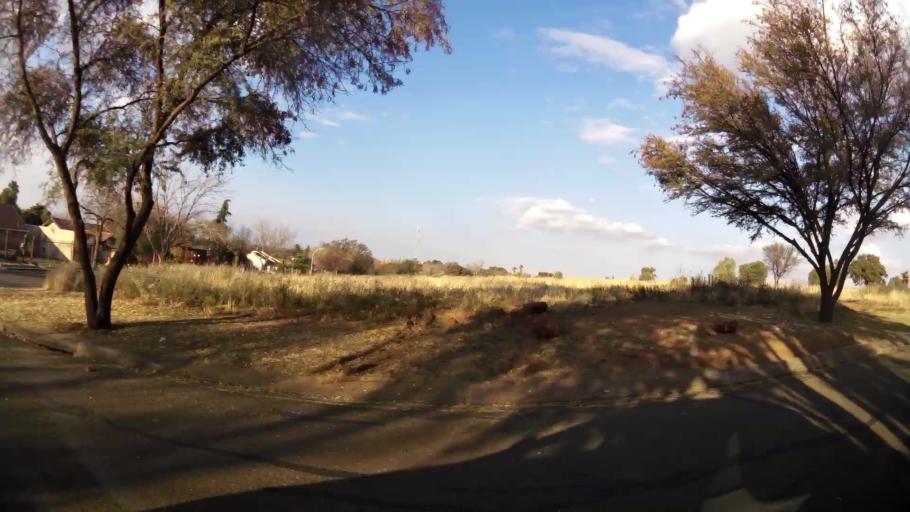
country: ZA
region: Orange Free State
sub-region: Mangaung Metropolitan Municipality
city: Bloemfontein
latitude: -29.1499
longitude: 26.1807
